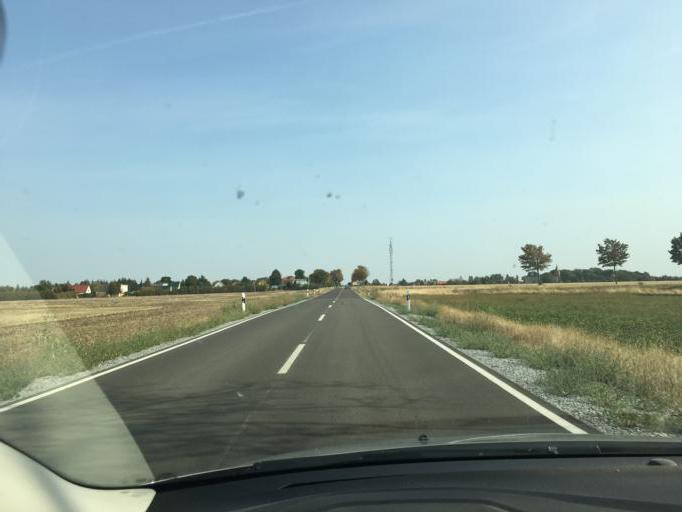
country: DE
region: Saxony-Anhalt
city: Wulfen
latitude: 51.7896
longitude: 11.8754
